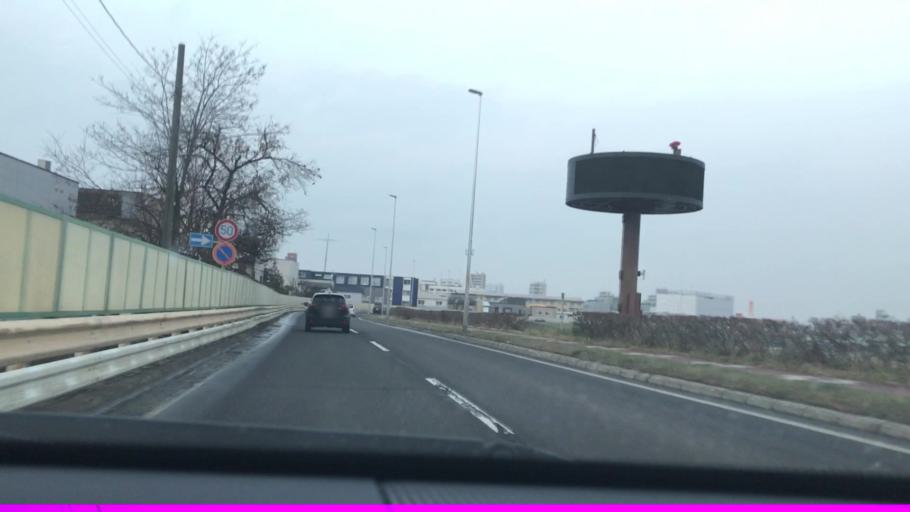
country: JP
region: Hokkaido
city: Sapporo
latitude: 43.0255
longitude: 141.3516
